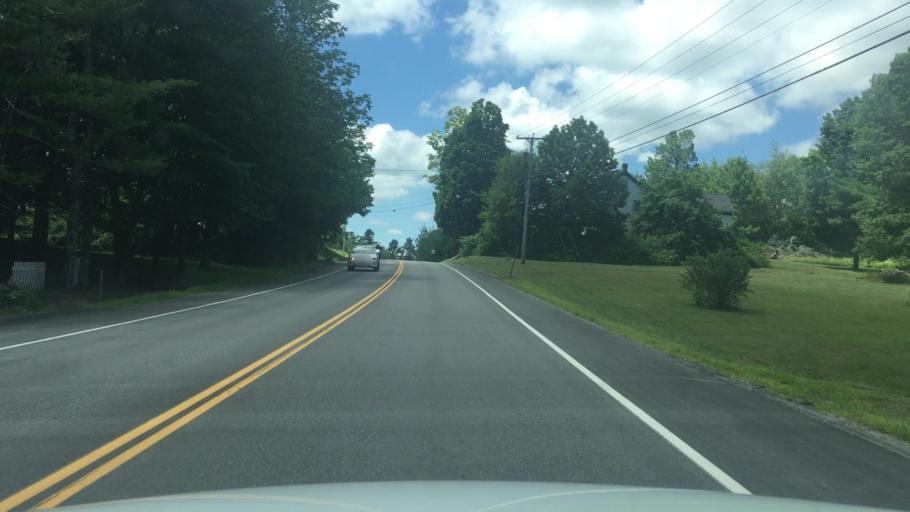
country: US
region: Maine
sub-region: Waldo County
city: Belfast
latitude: 44.4170
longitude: -69.0438
